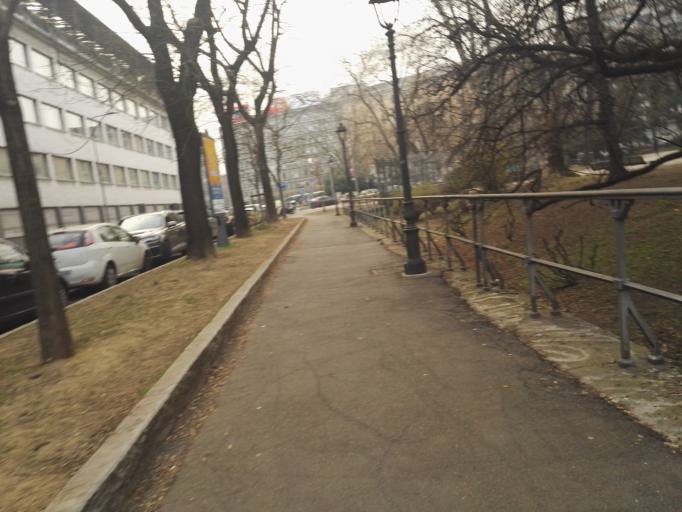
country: IT
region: Lombardy
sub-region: Citta metropolitana di Milano
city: Milano
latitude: 45.4730
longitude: 9.1972
